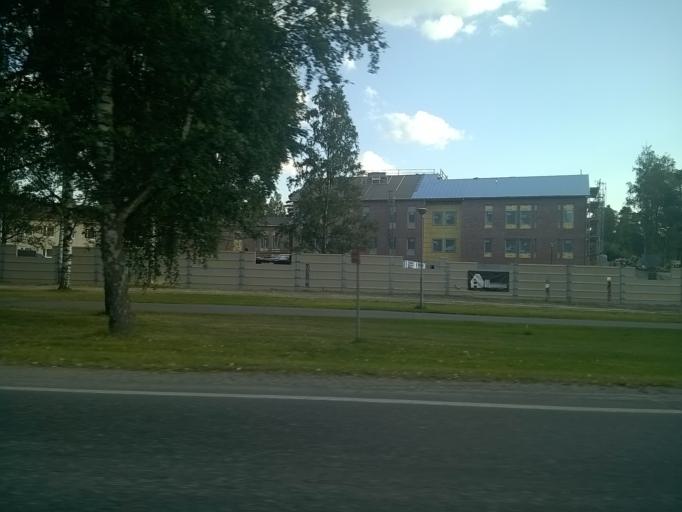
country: FI
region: Pirkanmaa
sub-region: Tampere
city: Tampere
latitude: 61.5043
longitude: 23.8221
